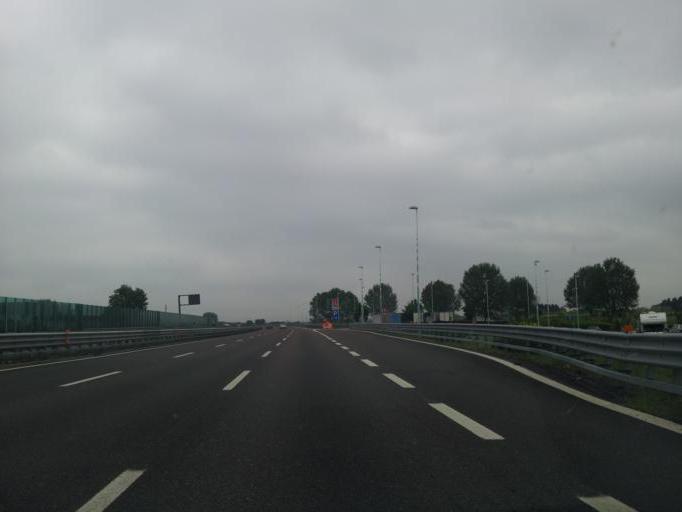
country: IT
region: Veneto
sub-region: Provincia di Verona
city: Monteforte d'Alpone
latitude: 45.4087
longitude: 11.2663
